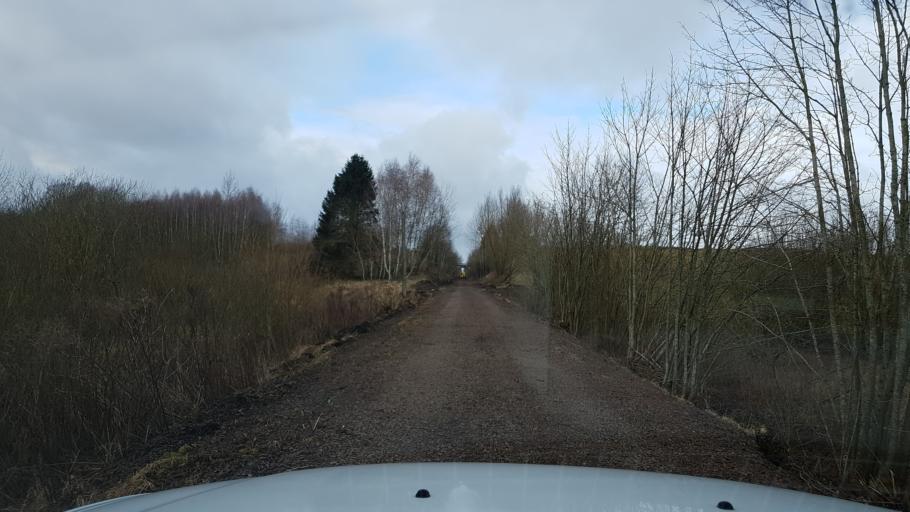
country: PL
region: West Pomeranian Voivodeship
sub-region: Powiat swidwinski
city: Polczyn-Zdroj
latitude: 53.7793
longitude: 16.0737
